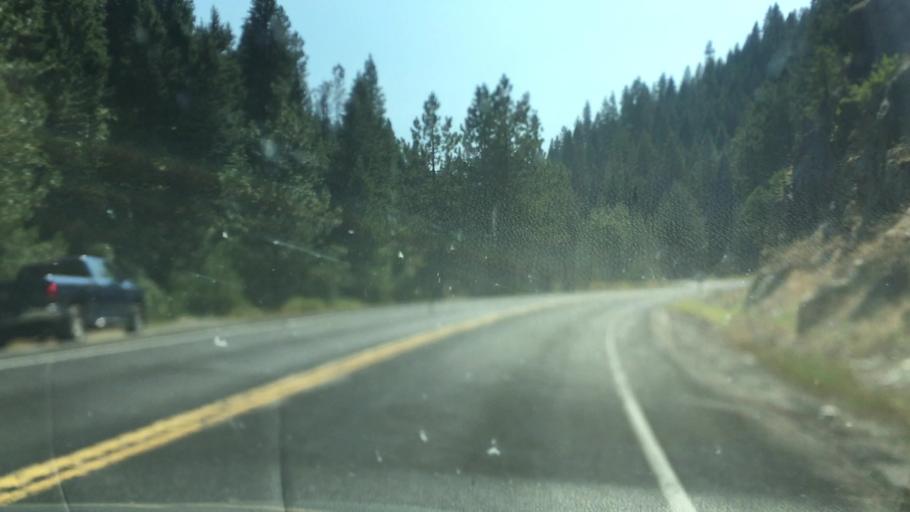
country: US
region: Idaho
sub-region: Valley County
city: Cascade
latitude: 44.2552
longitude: -116.0836
